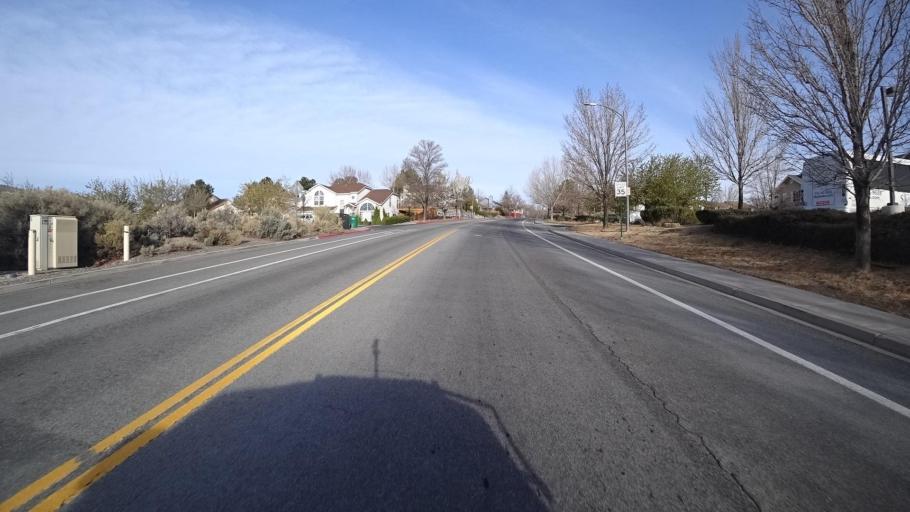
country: US
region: Nevada
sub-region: Washoe County
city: Reno
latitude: 39.5186
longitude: -119.8541
